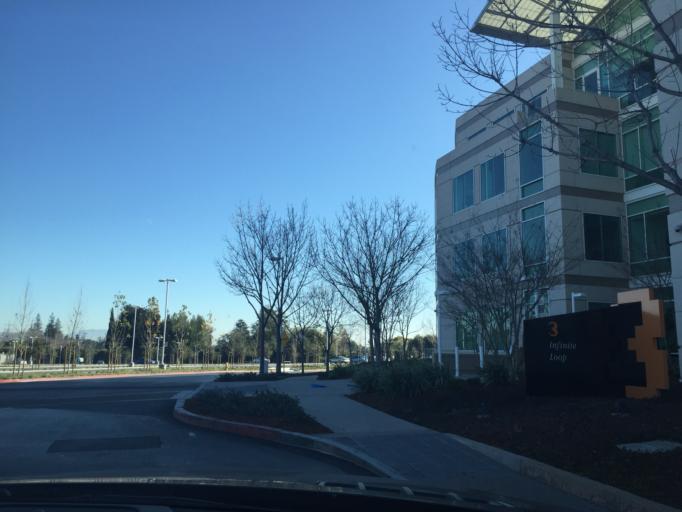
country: US
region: California
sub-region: Santa Clara County
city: Cupertino
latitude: 37.3335
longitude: -122.0296
